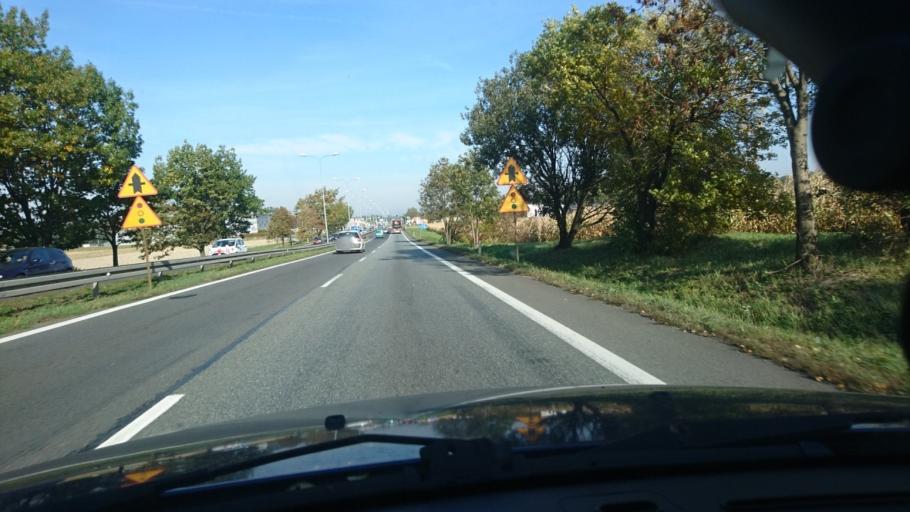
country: PL
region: Silesian Voivodeship
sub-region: Powiat pszczynski
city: Goczalkowice Zdroj
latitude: 49.9535
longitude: 18.9670
